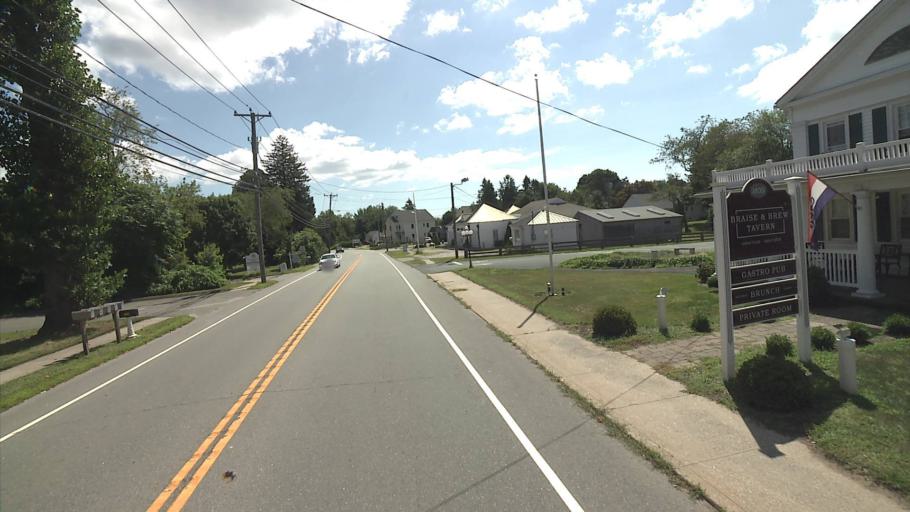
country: US
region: Connecticut
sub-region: Middlesex County
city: Westbrook Center
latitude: 41.2806
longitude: -72.4275
